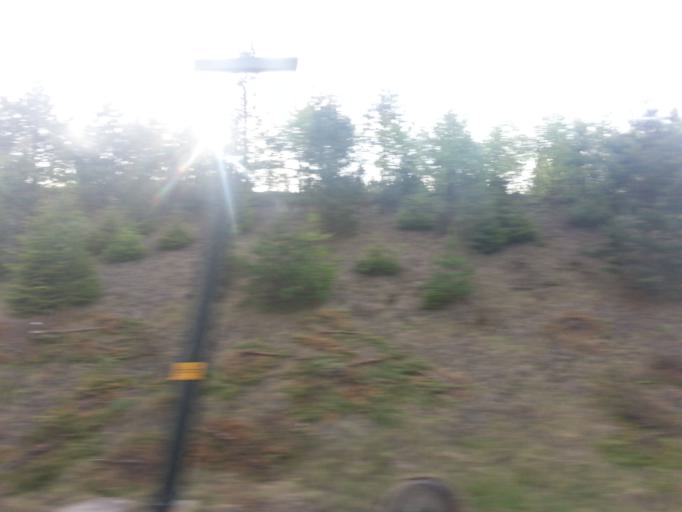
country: NO
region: Akershus
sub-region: Ullensaker
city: Jessheim
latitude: 60.1520
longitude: 11.1480
